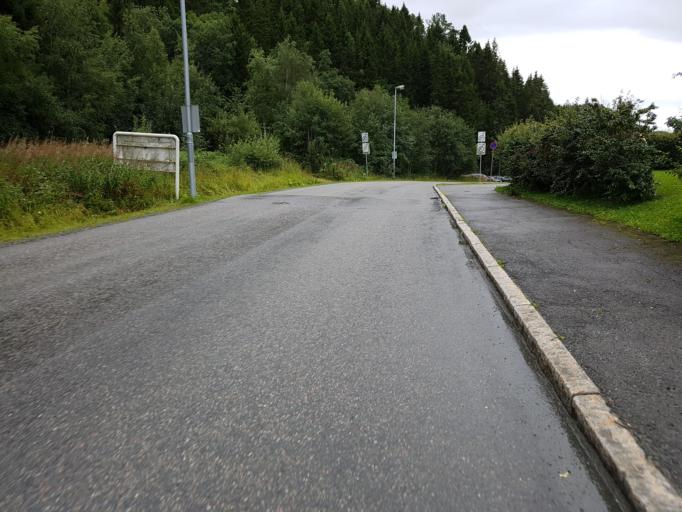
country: NO
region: Sor-Trondelag
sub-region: Trondheim
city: Trondheim
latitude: 63.4056
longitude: 10.4848
